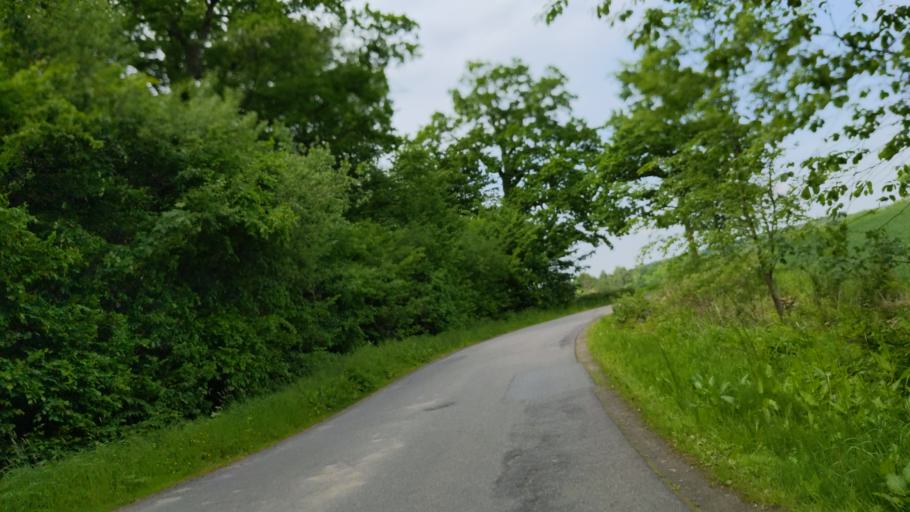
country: DE
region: Schleswig-Holstein
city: Ratekau
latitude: 53.9559
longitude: 10.7049
